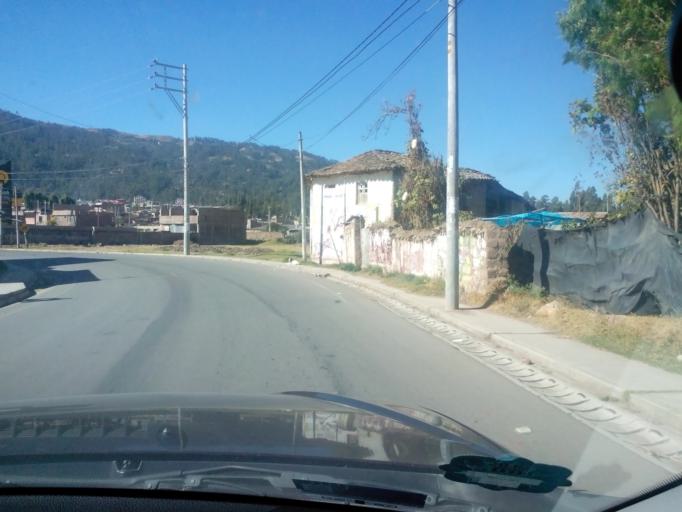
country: PE
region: Apurimac
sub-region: Provincia de Andahuaylas
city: Talavera
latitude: -13.6595
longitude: -73.4310
